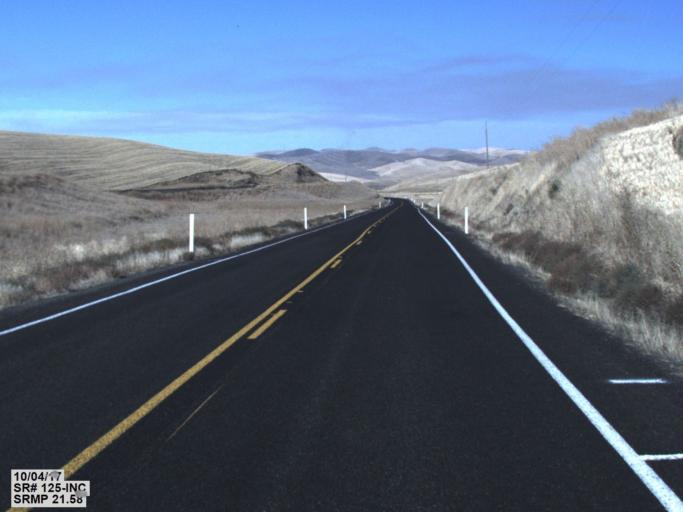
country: US
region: Washington
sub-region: Walla Walla County
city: Waitsburg
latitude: 46.2701
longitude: -118.3502
